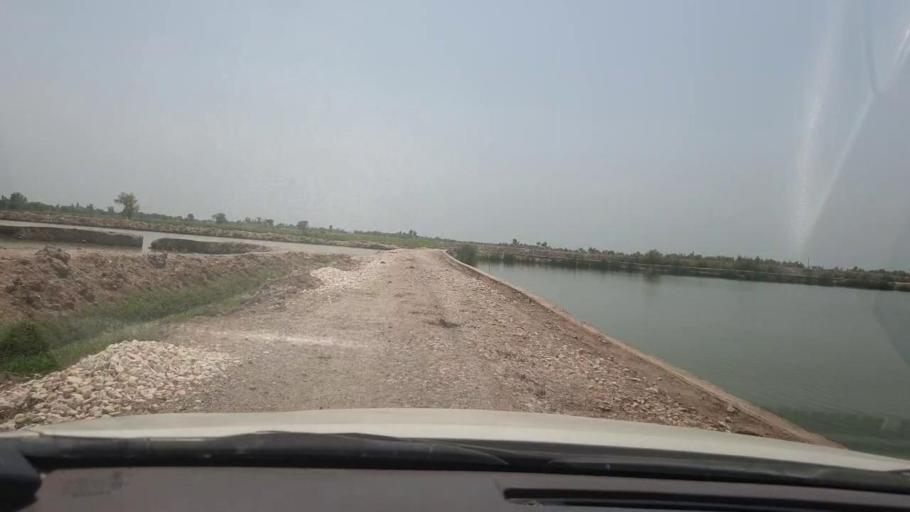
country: PK
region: Sindh
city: Garhi Yasin
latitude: 27.9066
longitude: 68.5535
